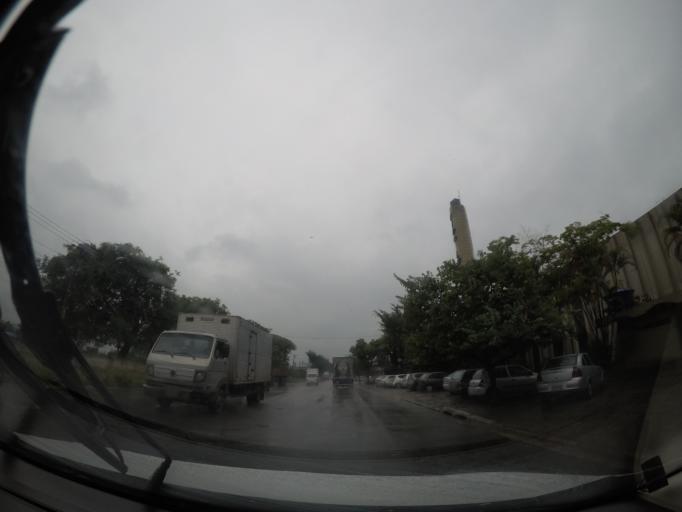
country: BR
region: Sao Paulo
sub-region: Guarulhos
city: Guarulhos
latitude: -23.4768
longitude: -46.4718
